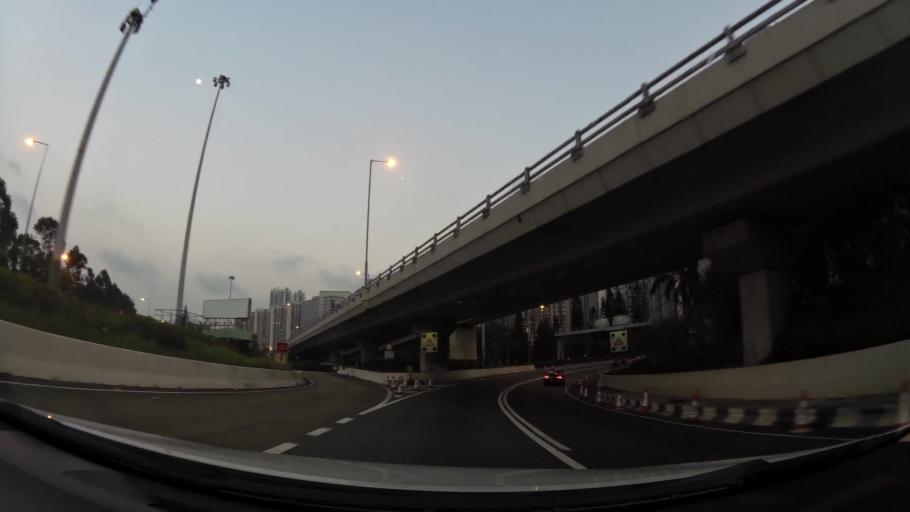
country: HK
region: Kowloon City
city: Kowloon
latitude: 22.2900
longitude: 114.2139
